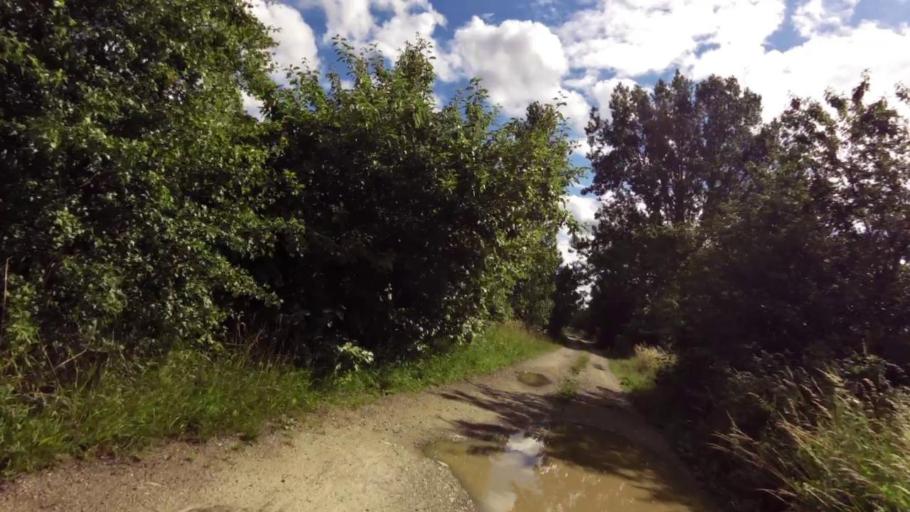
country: PL
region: West Pomeranian Voivodeship
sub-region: Powiat slawienski
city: Slawno
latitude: 54.5111
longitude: 16.7060
